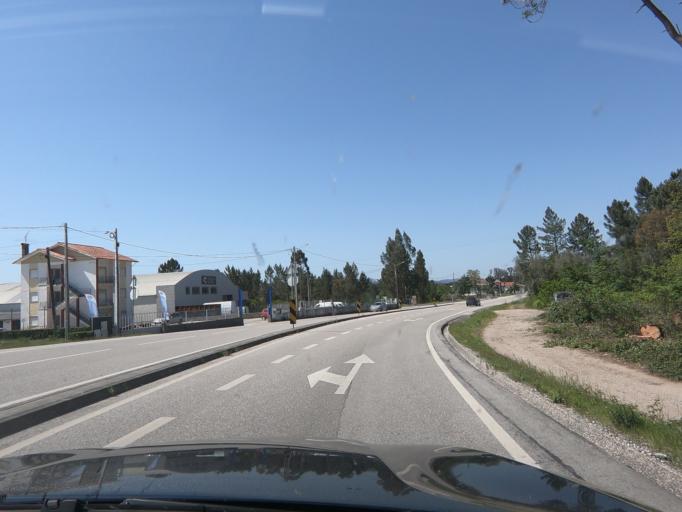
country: PT
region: Coimbra
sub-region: Lousa
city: Lousa
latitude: 40.1303
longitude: -8.2496
